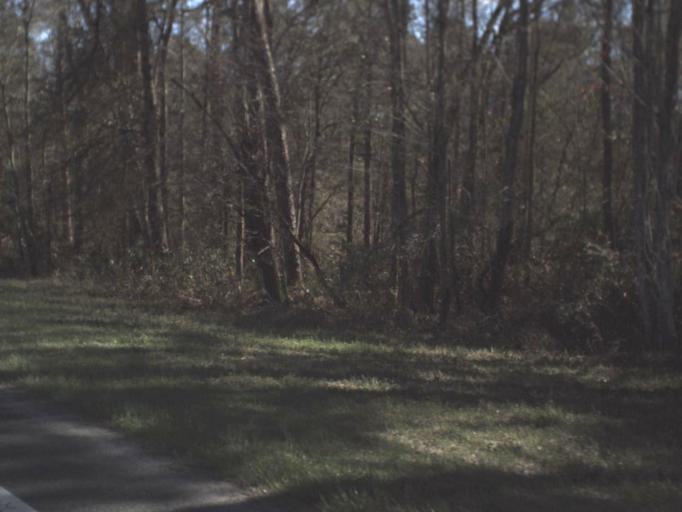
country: US
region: Florida
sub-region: Gadsden County
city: Midway
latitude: 30.4828
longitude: -84.4194
